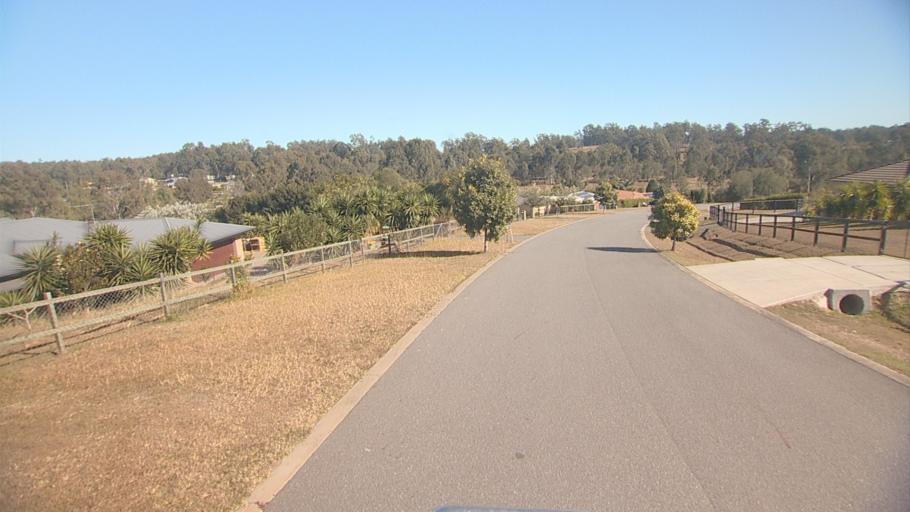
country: AU
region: Queensland
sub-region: Logan
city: Cedar Vale
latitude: -27.8696
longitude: 153.0022
